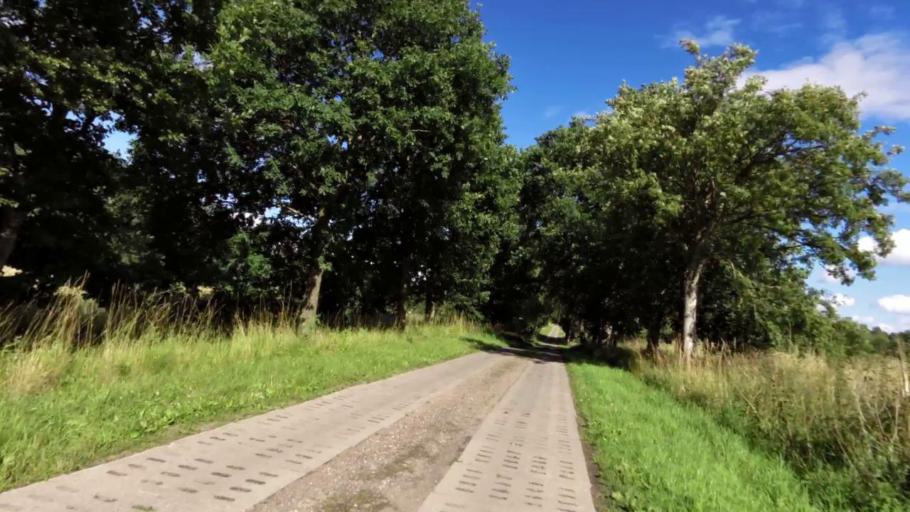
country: PL
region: West Pomeranian Voivodeship
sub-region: Powiat slawienski
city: Slawno
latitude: 54.4635
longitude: 16.7180
